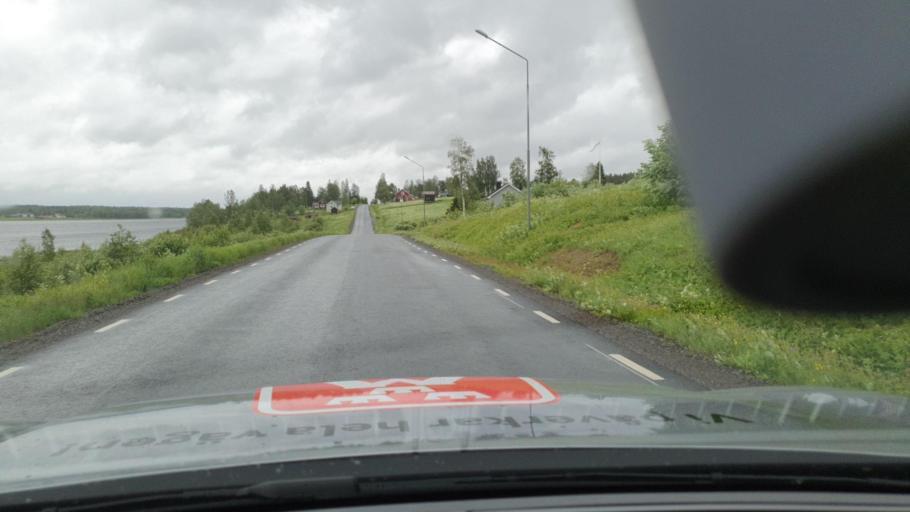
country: FI
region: Lapland
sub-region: Torniolaakso
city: Ylitornio
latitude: 66.1838
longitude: 23.7722
